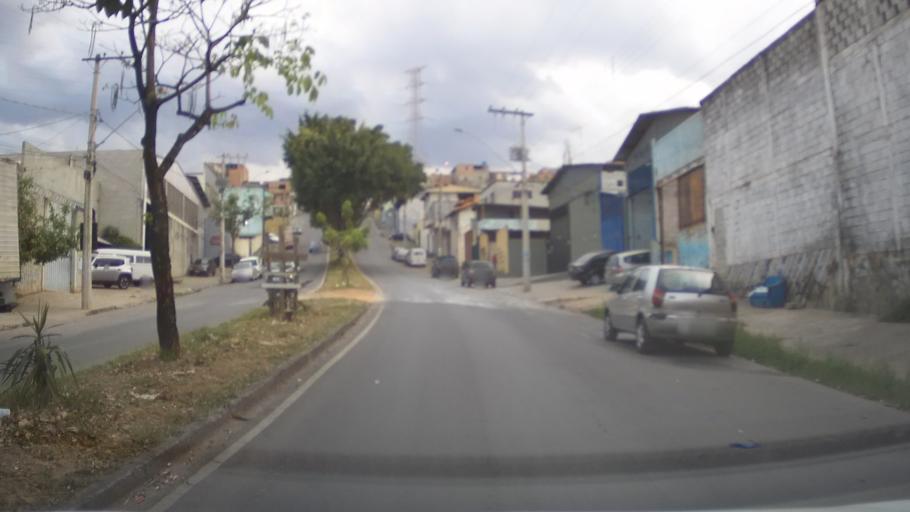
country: BR
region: Minas Gerais
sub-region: Belo Horizonte
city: Belo Horizonte
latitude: -19.8740
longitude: -43.9020
